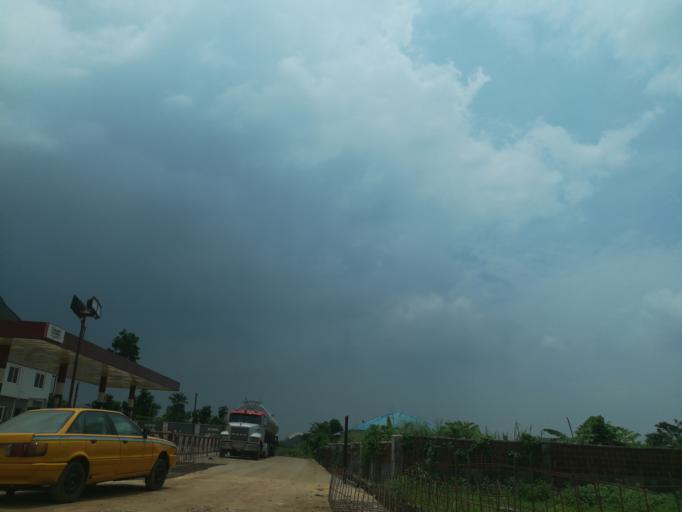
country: NG
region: Lagos
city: Ikorodu
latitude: 6.6146
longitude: 3.5712
